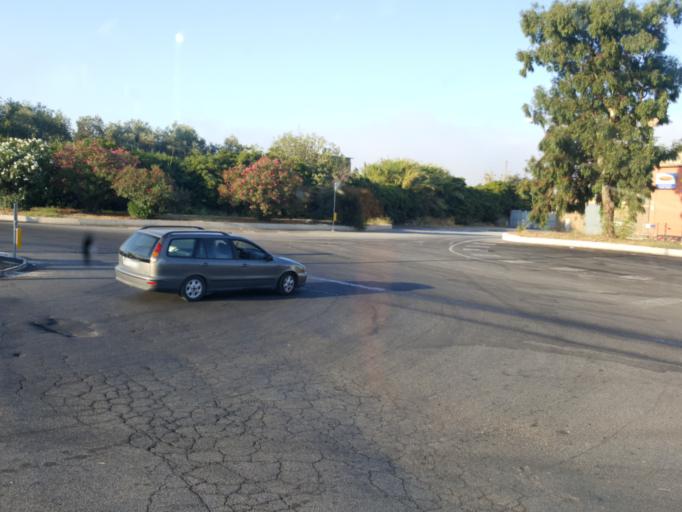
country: IT
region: Latium
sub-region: Citta metropolitana di Roma Capitale
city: Aurelia
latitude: 42.1183
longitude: 11.7701
